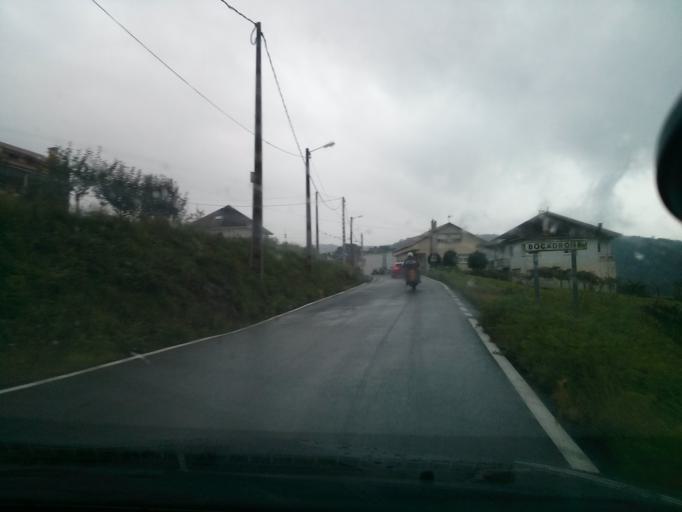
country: ES
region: Galicia
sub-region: Provincia da Coruna
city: Outes
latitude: 42.8318
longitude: -8.8711
